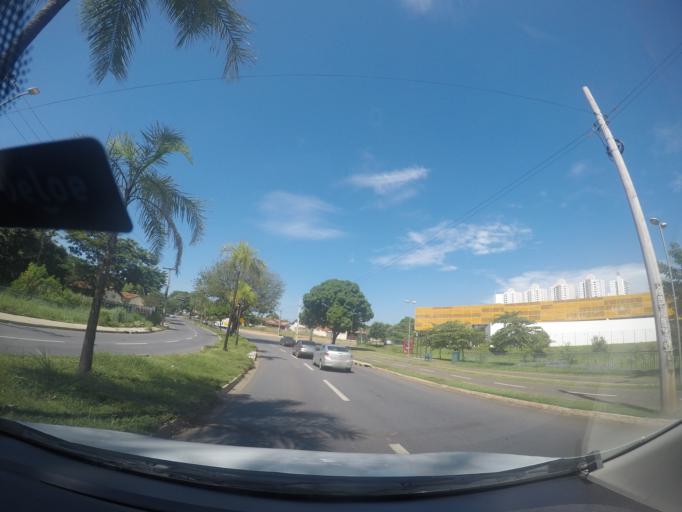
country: BR
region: Goias
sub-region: Goiania
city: Goiania
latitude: -16.7129
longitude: -49.3181
